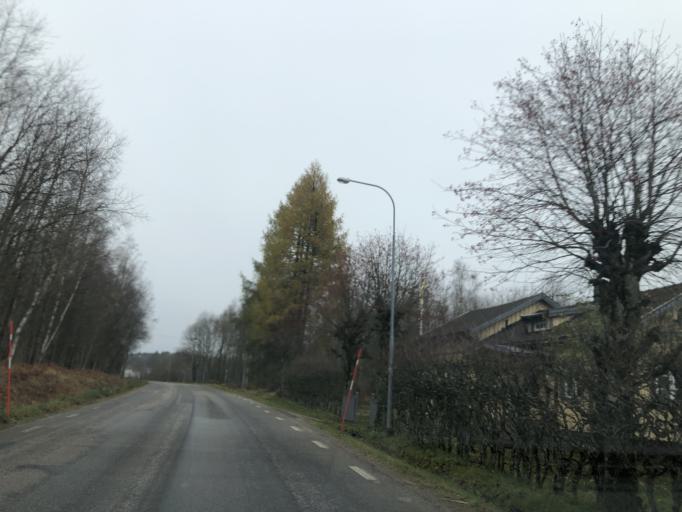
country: SE
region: Vaestra Goetaland
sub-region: Ulricehamns Kommun
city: Ulricehamn
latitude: 57.6954
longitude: 13.4934
